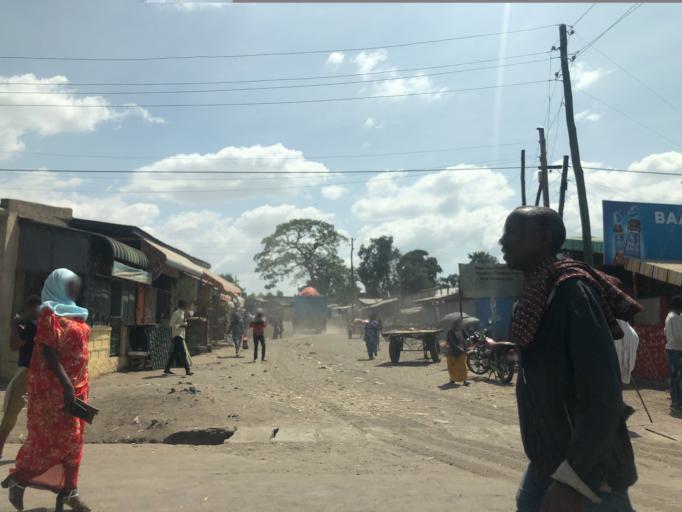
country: ET
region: Oromiya
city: Shashemene
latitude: 7.2105
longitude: 38.6166
